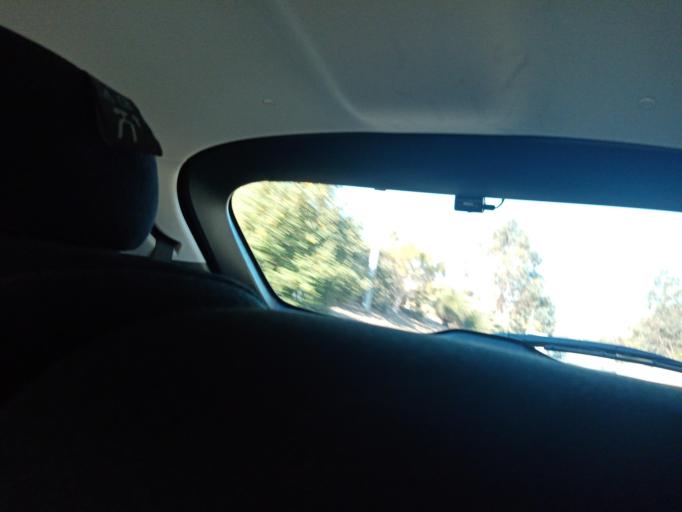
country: AU
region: Western Australia
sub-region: City of Cockburn
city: Yangebup
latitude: -32.1274
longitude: 115.8272
